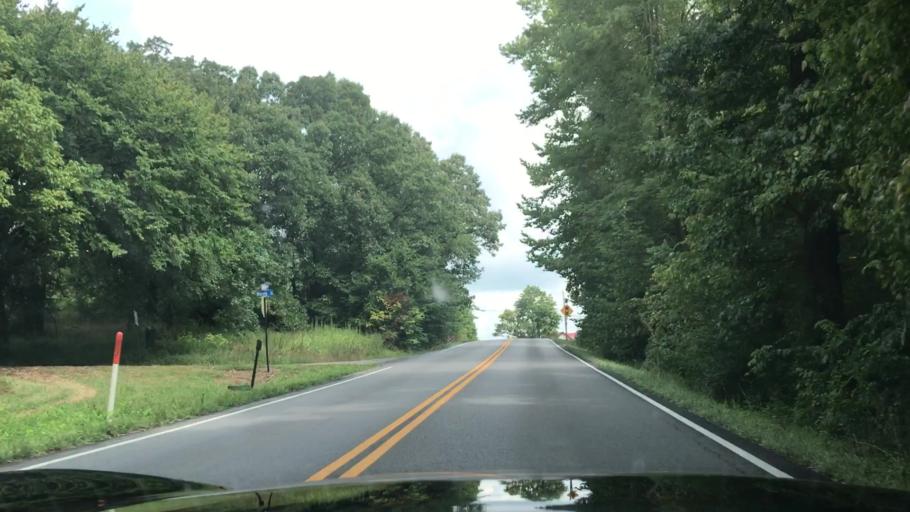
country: US
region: Kentucky
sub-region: Muhlenberg County
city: Central City
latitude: 37.2155
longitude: -87.0449
